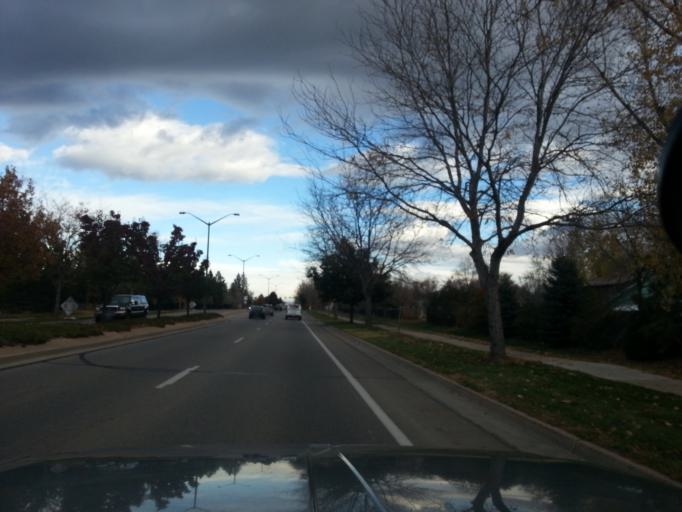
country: US
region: Colorado
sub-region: Larimer County
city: Fort Collins
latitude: 40.5407
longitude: -105.1151
